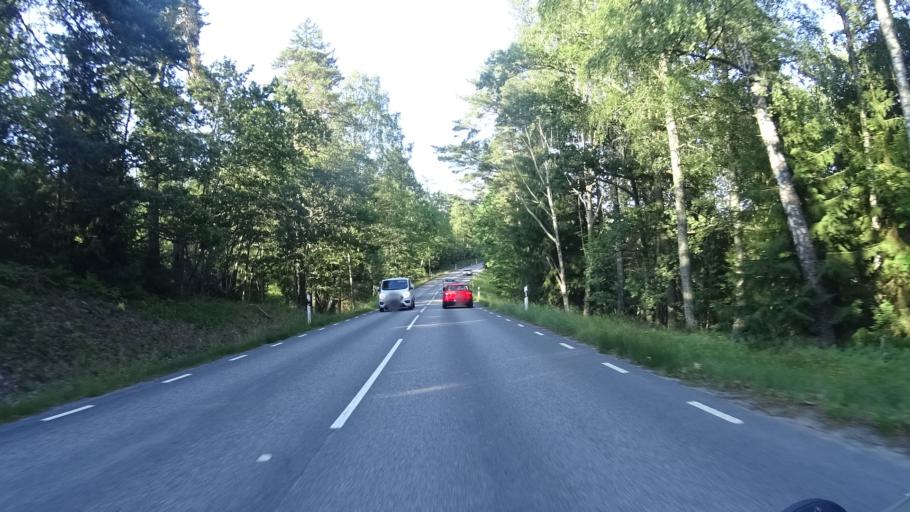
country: SE
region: Stockholm
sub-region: Sodertalje Kommun
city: Pershagen
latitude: 59.1184
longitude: 17.6437
